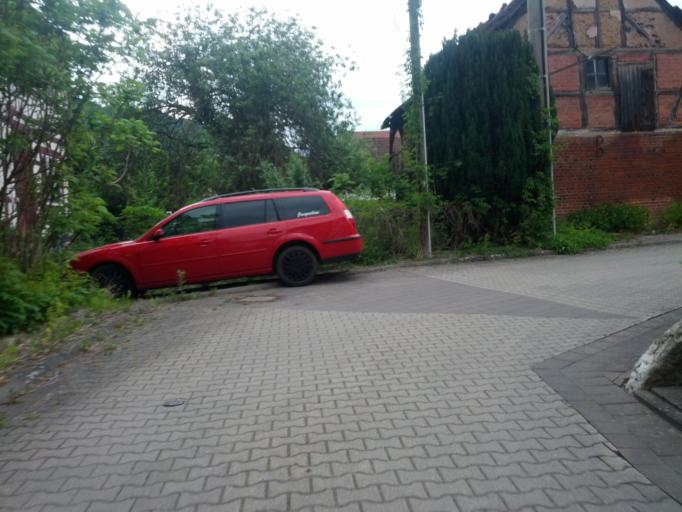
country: DE
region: Thuringia
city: Frankenroda
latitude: 51.0960
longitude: 10.2748
